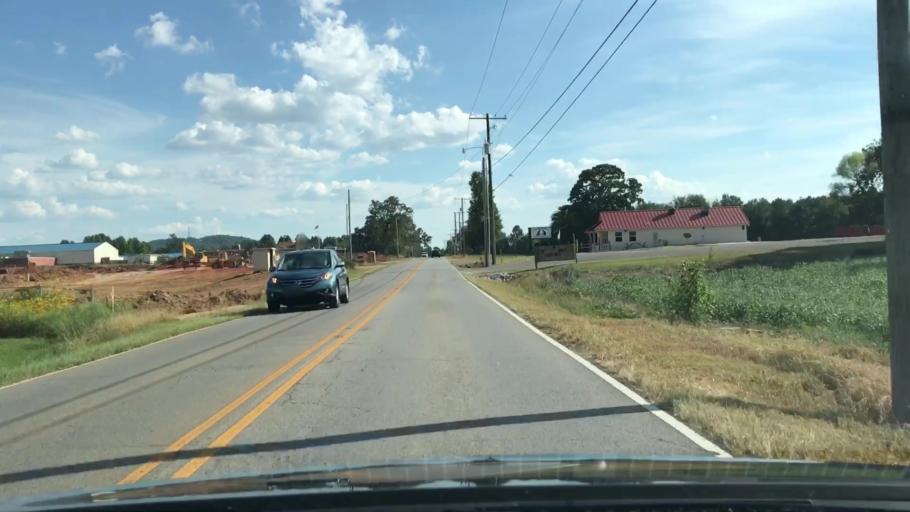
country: US
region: Alabama
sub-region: Madison County
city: Harvest
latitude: 34.8513
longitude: -86.7492
